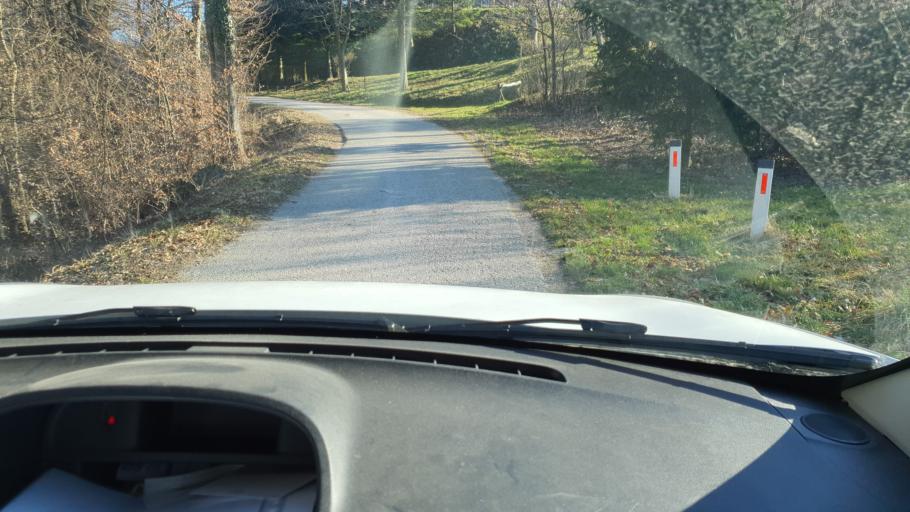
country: SI
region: Sveti Andraz v Slovenskih Goricah
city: Vitomarci
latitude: 46.5259
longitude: 15.9308
